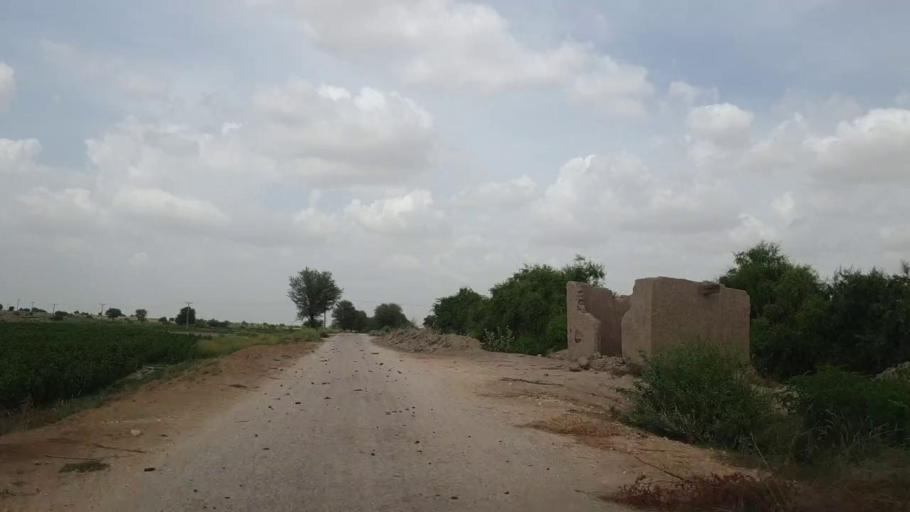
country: PK
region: Sindh
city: Kot Diji
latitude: 27.2236
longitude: 69.0856
